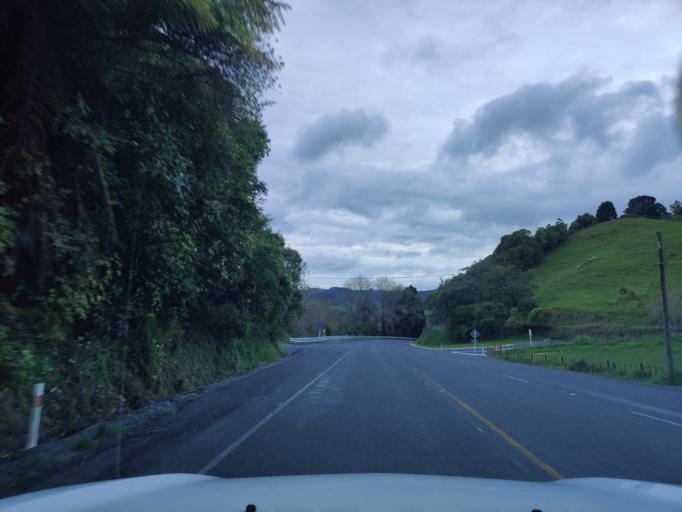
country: NZ
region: Waikato
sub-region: Otorohanga District
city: Otorohanga
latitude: -38.3512
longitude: 175.1613
